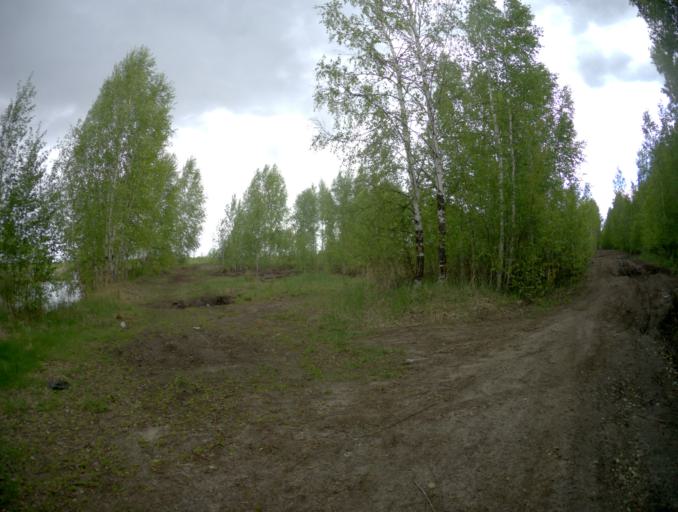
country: RU
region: Moskovskaya
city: Cherusti
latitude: 55.5878
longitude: 40.1186
